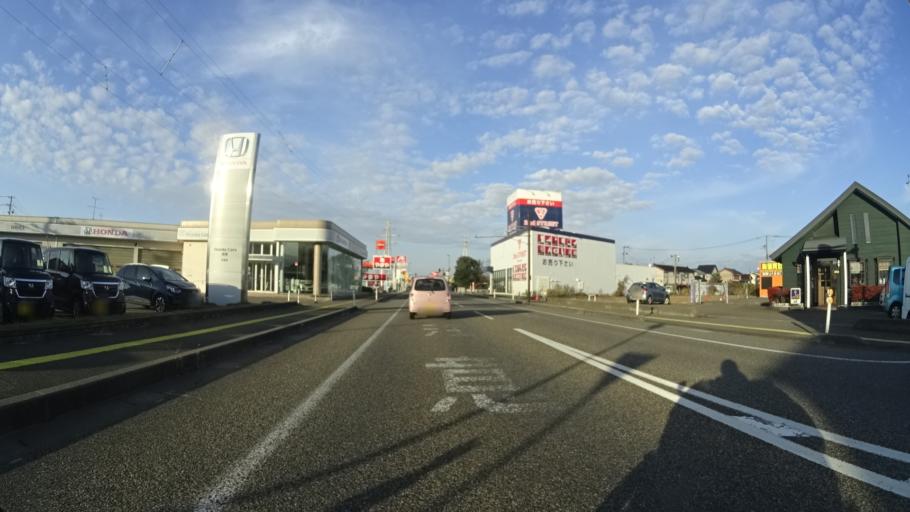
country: JP
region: Niigata
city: Kashiwazaki
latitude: 37.3736
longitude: 138.5789
